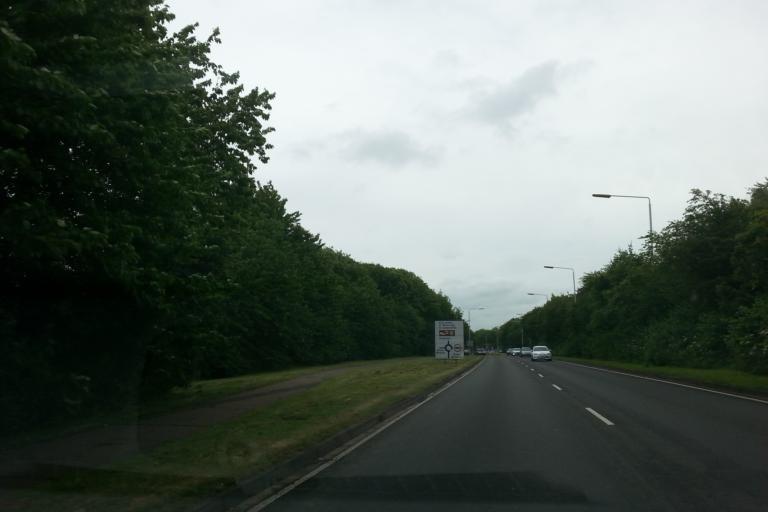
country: GB
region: England
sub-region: Peterborough
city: Castor
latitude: 52.5537
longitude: -0.3075
